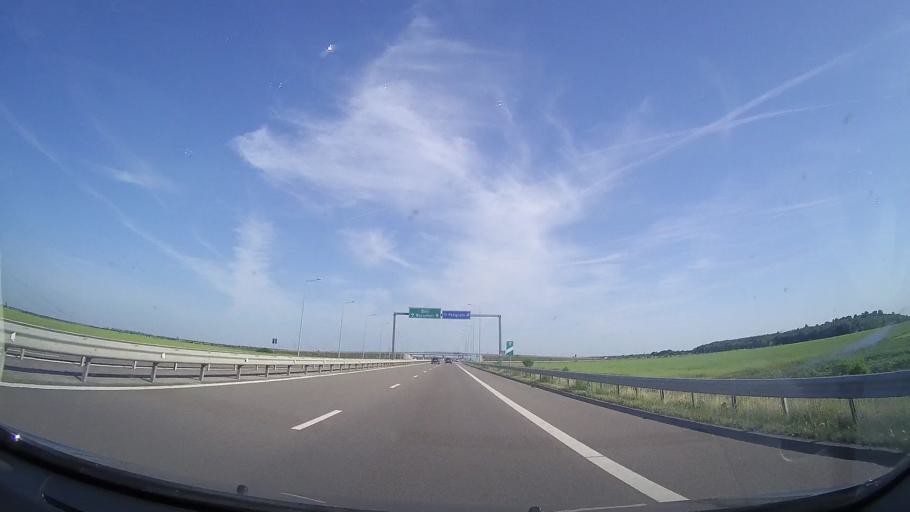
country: RO
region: Prahova
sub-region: Comuna Olari
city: Olari
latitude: 44.7813
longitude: 26.2451
